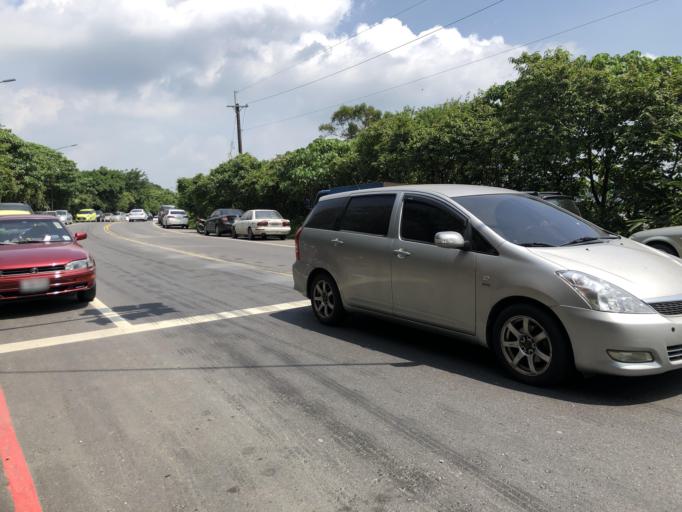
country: TW
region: Taiwan
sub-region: Keelung
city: Keelung
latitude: 25.0769
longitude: 121.6820
